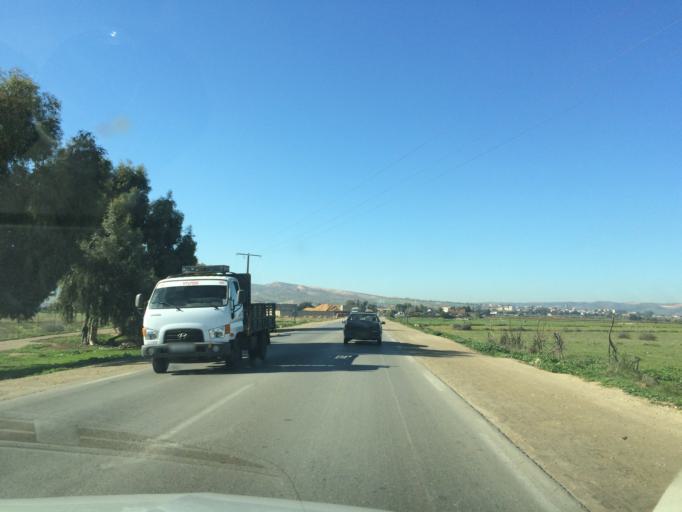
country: DZ
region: Relizane
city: Relizane
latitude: 35.8992
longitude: 0.5357
